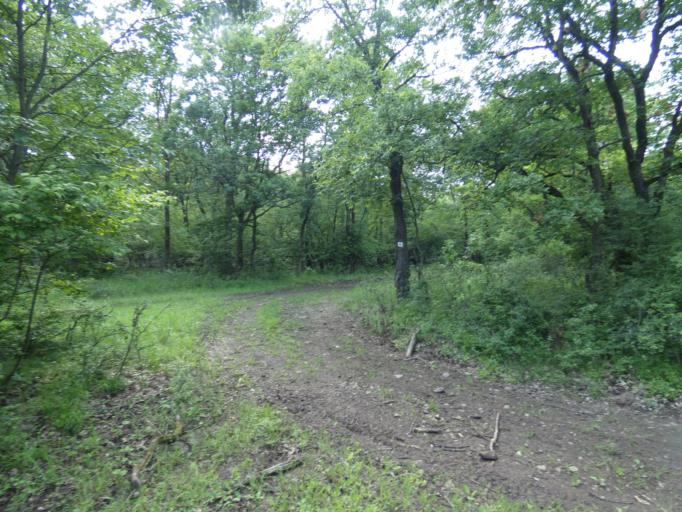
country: HU
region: Pest
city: Szob
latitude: 47.8585
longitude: 18.8380
